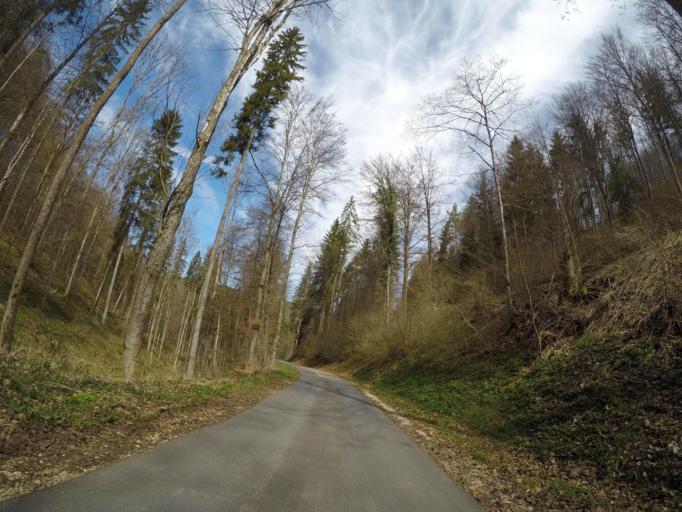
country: DE
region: Baden-Wuerttemberg
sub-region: Tuebingen Region
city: Mehrstetten
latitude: 48.3633
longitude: 9.6212
